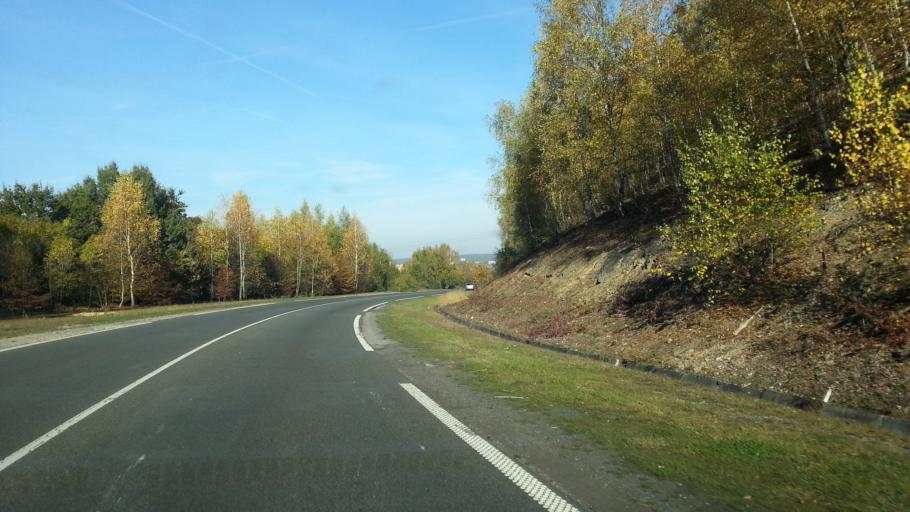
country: FR
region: Picardie
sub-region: Departement de l'Oise
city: Thiverny
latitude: 49.2471
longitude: 2.4565
